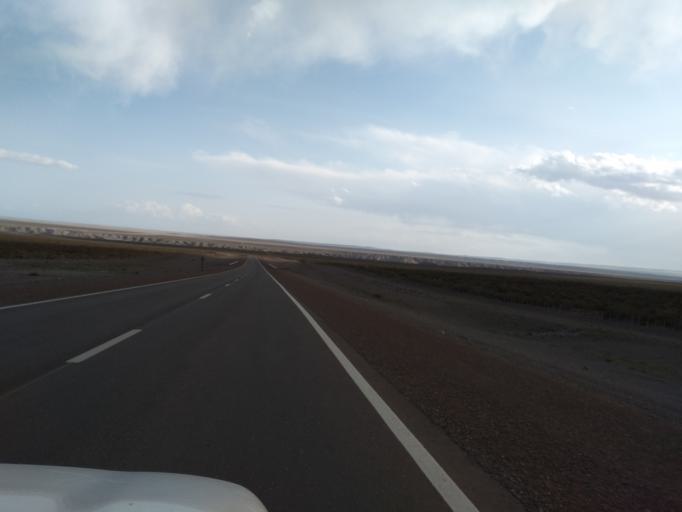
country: AR
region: Mendoza
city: San Rafael
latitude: -34.6068
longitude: -69.1814
